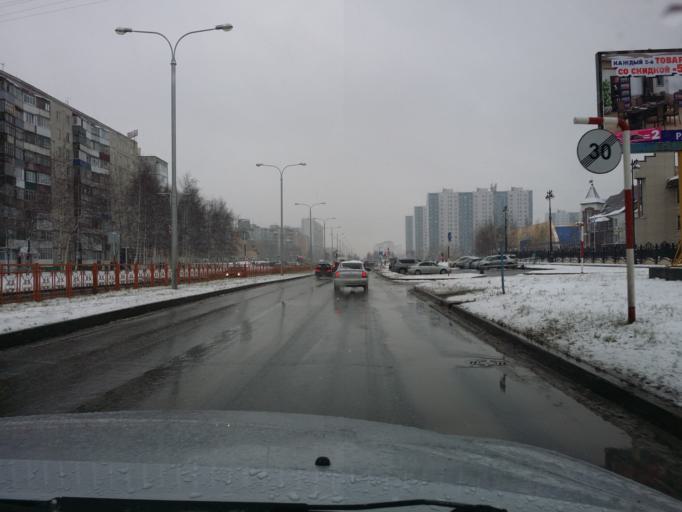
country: RU
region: Khanty-Mansiyskiy Avtonomnyy Okrug
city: Nizhnevartovsk
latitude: 60.9422
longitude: 76.5984
